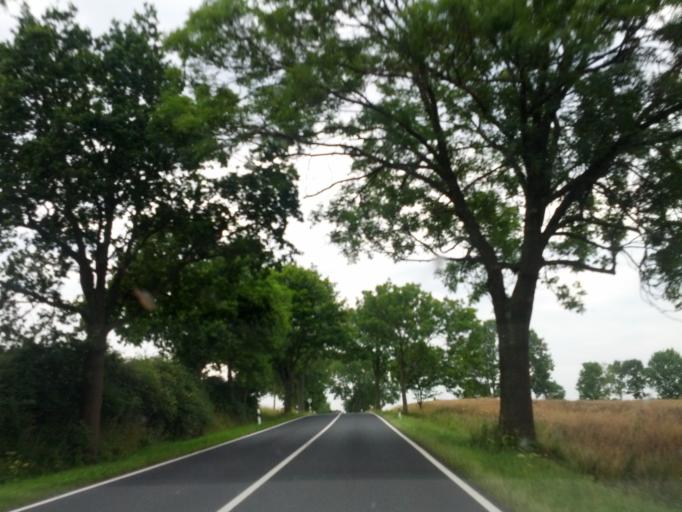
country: DE
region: Mecklenburg-Vorpommern
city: Satow-Oberhagen
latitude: 53.9799
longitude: 11.8620
